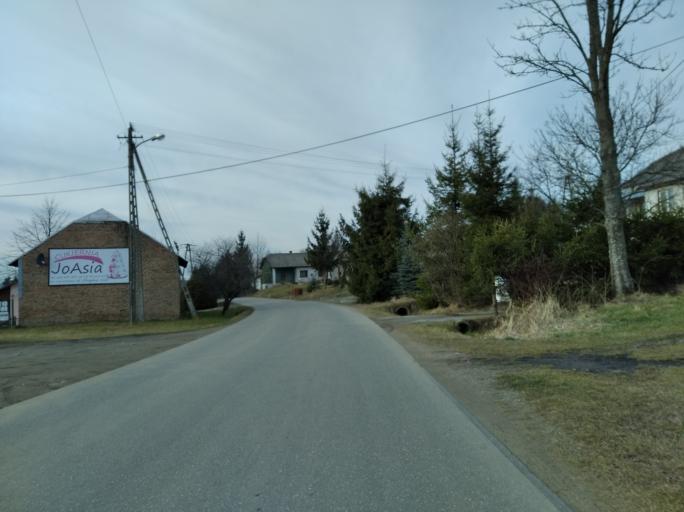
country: PL
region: Subcarpathian Voivodeship
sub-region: Powiat brzozowski
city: Gorki
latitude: 49.6478
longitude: 22.0386
